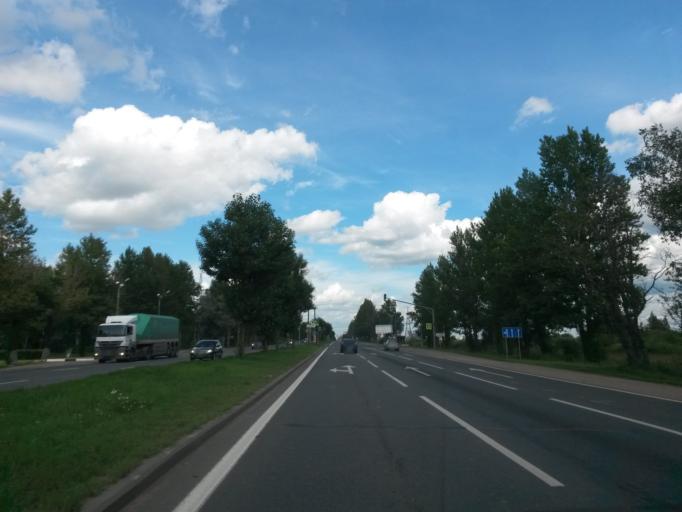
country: RU
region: Jaroslavl
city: Krasnyye Tkachi
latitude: 57.5527
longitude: 39.8127
